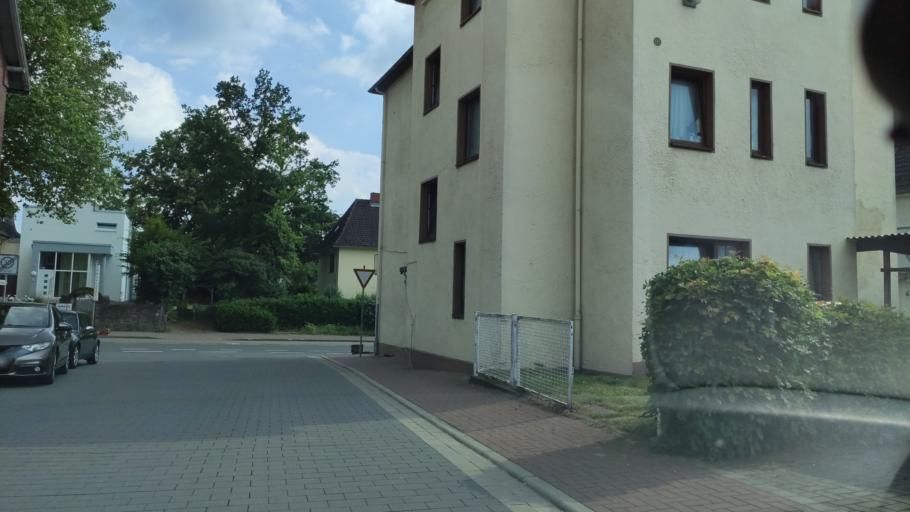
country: DE
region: Lower Saxony
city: Holzminden
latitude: 51.8284
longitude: 9.4649
